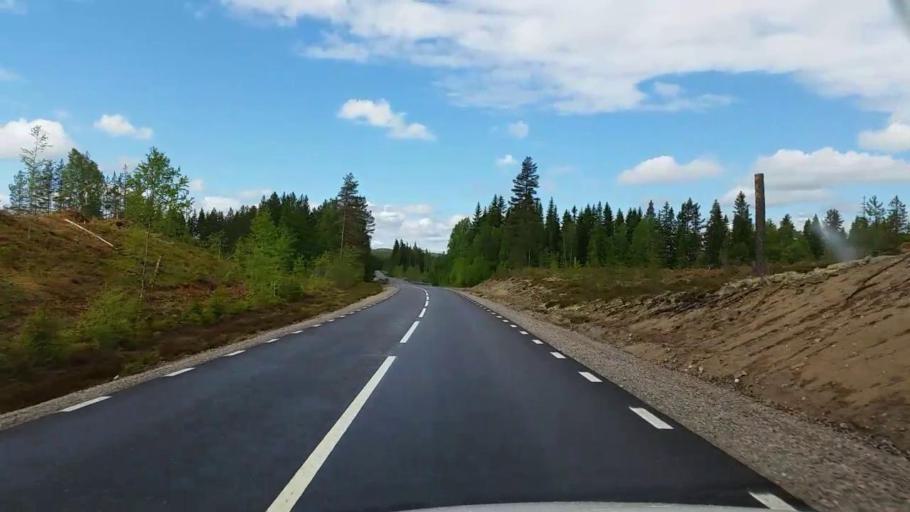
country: SE
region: Gaevleborg
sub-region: Sandvikens Kommun
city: Jarbo
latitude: 60.8768
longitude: 16.3975
